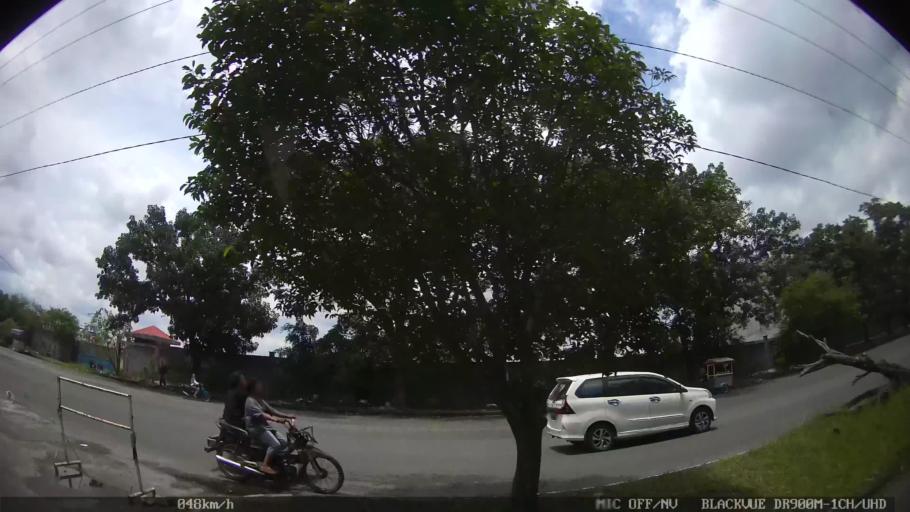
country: ID
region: North Sumatra
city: Medan
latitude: 3.6087
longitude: 98.7121
